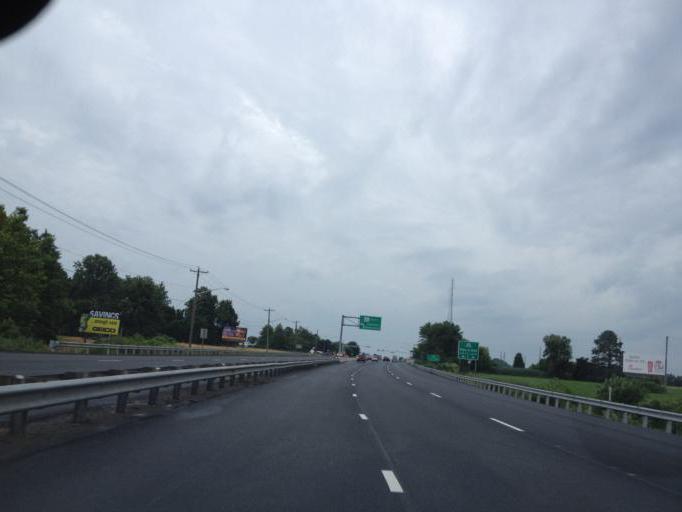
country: US
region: Maryland
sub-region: Queen Anne's County
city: Centreville
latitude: 38.9427
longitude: -76.0627
